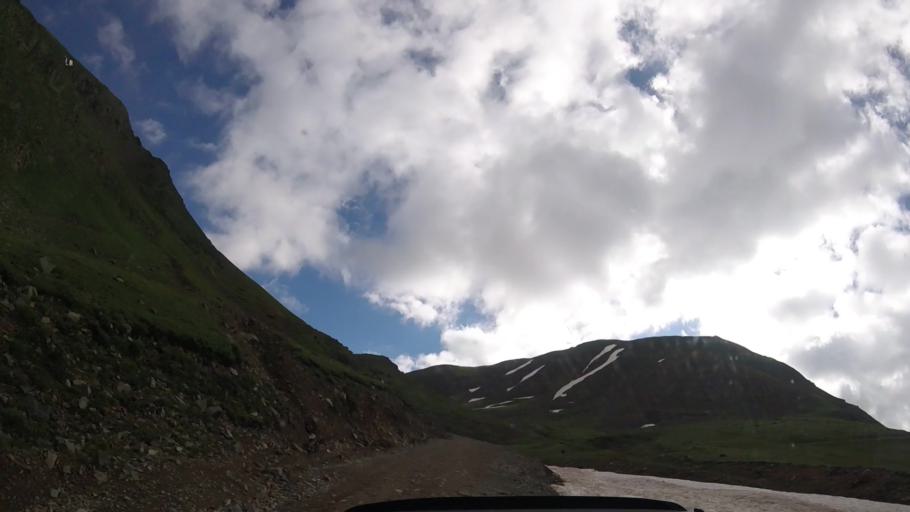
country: US
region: Colorado
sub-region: San Juan County
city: Silverton
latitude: 37.9130
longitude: -107.6318
